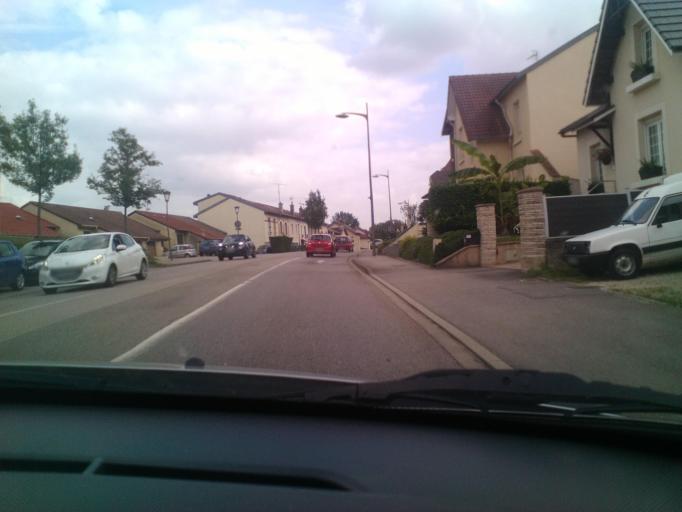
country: FR
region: Lorraine
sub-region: Departement de Meurthe-et-Moselle
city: Frouard
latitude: 48.7529
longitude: 6.1440
